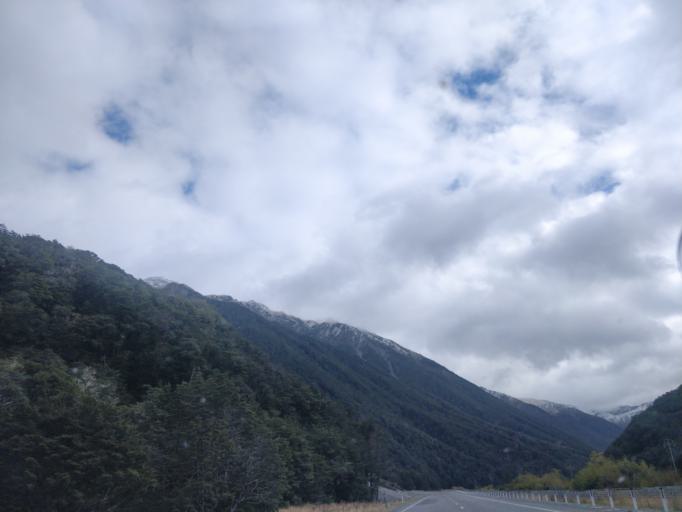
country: NZ
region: West Coast
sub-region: Grey District
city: Greymouth
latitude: -42.9767
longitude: 171.5883
